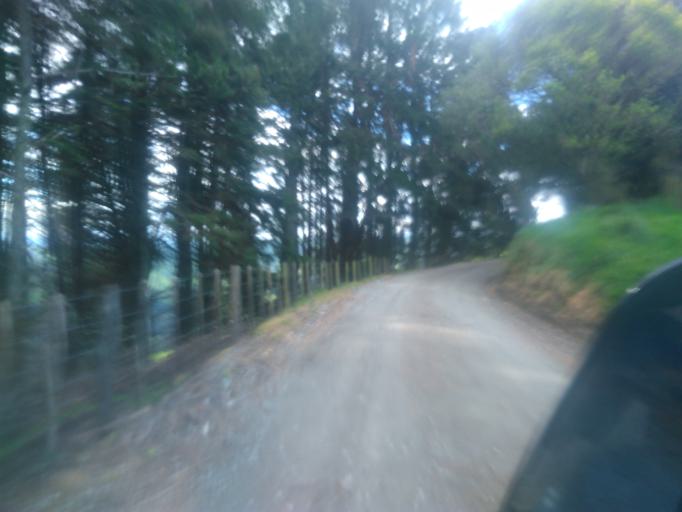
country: NZ
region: Hawke's Bay
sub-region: Wairoa District
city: Wairoa
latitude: -38.7729
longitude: 177.6376
